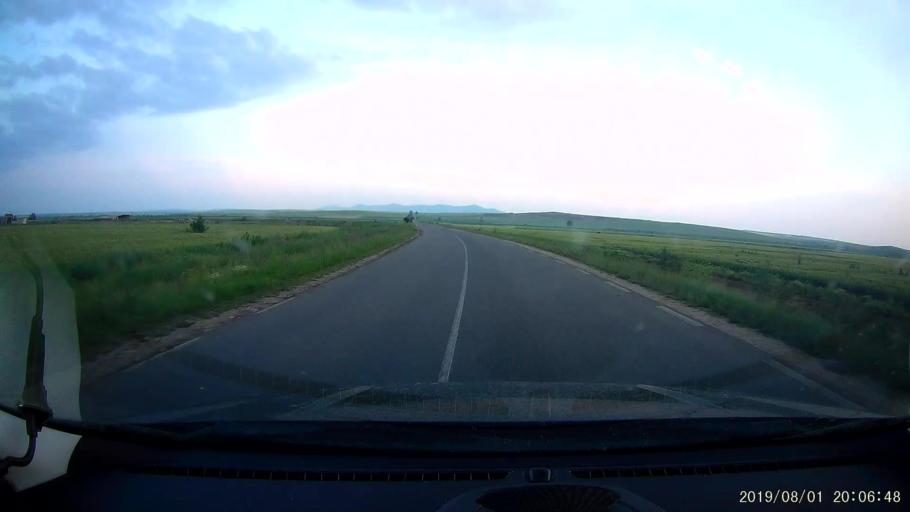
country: BG
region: Yambol
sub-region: Obshtina Yambol
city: Yambol
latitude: 42.5309
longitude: 26.5581
